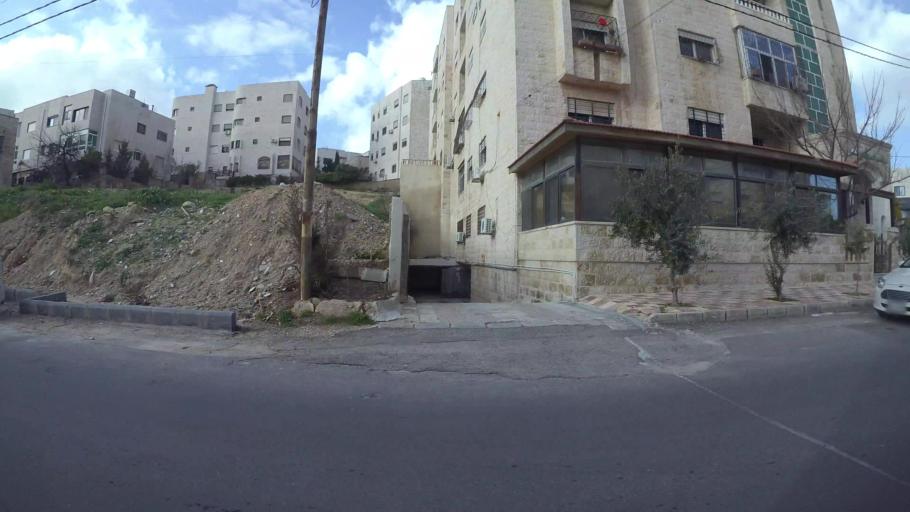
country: JO
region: Amman
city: Al Jubayhah
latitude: 31.9884
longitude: 35.8544
